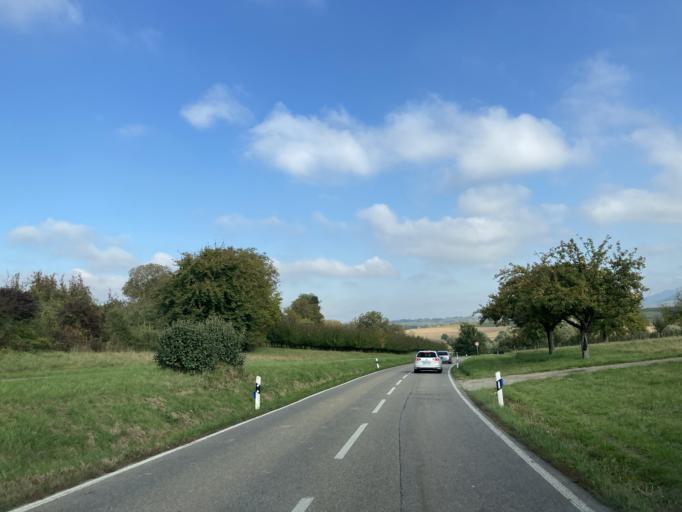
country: DE
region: Baden-Wuerttemberg
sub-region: Freiburg Region
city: Mullheim
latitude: 47.8212
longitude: 7.6474
